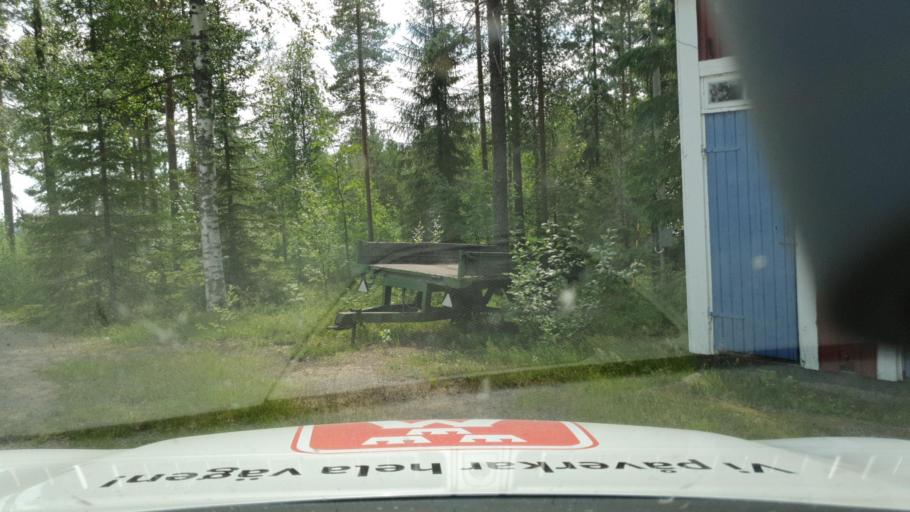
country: SE
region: Vaesterbotten
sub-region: Umea Kommun
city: Roback
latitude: 64.0134
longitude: 20.0804
